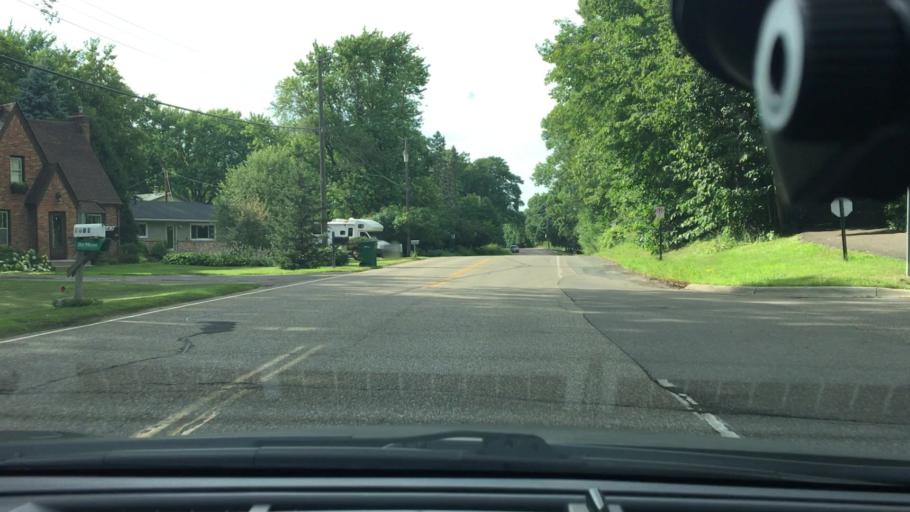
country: US
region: Minnesota
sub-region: Hennepin County
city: Plymouth
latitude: 45.0088
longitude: -93.4334
